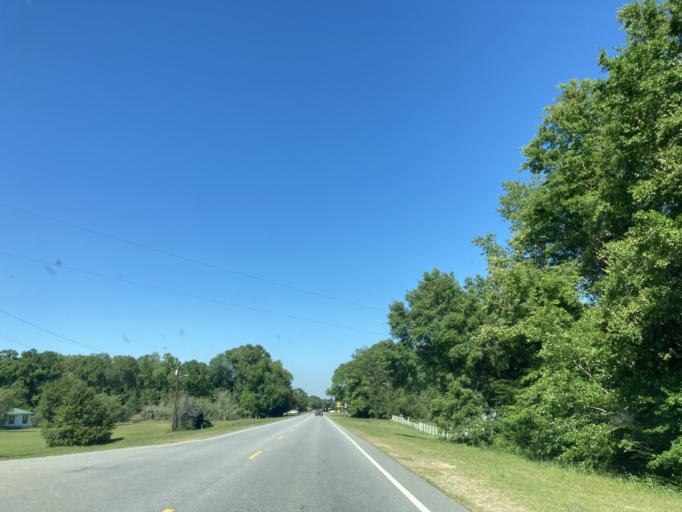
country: US
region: Georgia
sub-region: Baker County
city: Newton
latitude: 31.3228
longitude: -84.3428
